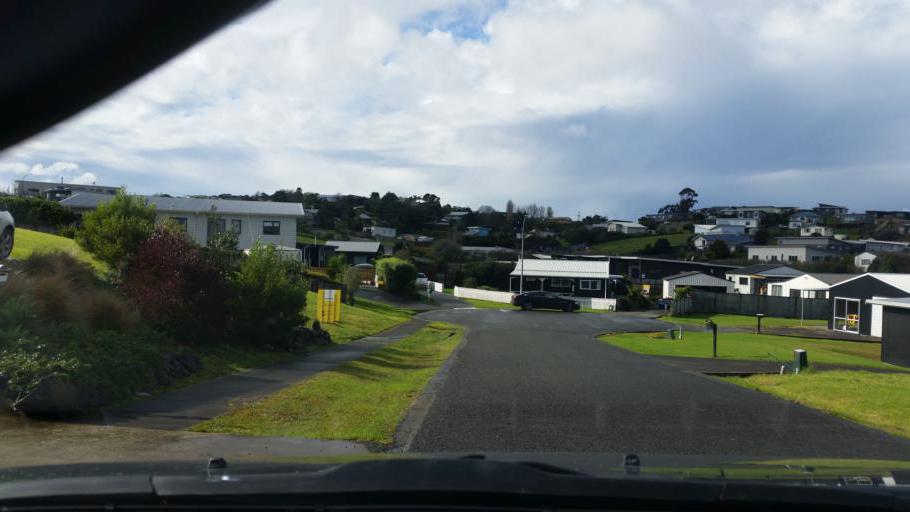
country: NZ
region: Auckland
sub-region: Auckland
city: Wellsford
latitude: -36.0882
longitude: 174.5774
